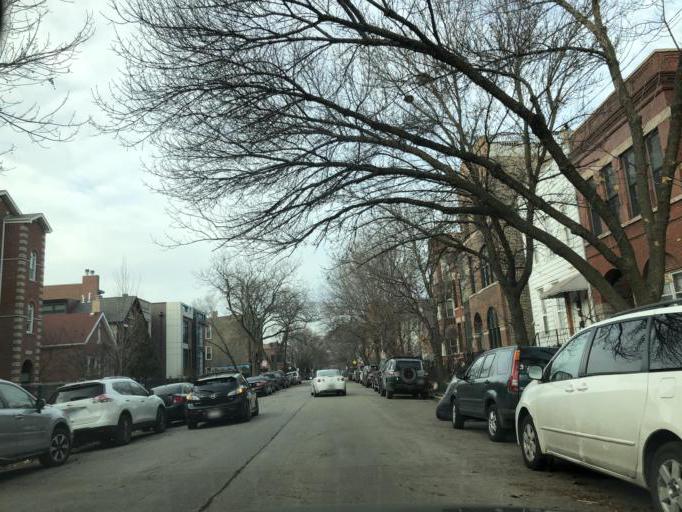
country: US
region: Illinois
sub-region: Cook County
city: Chicago
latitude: 41.8941
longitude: -87.6781
